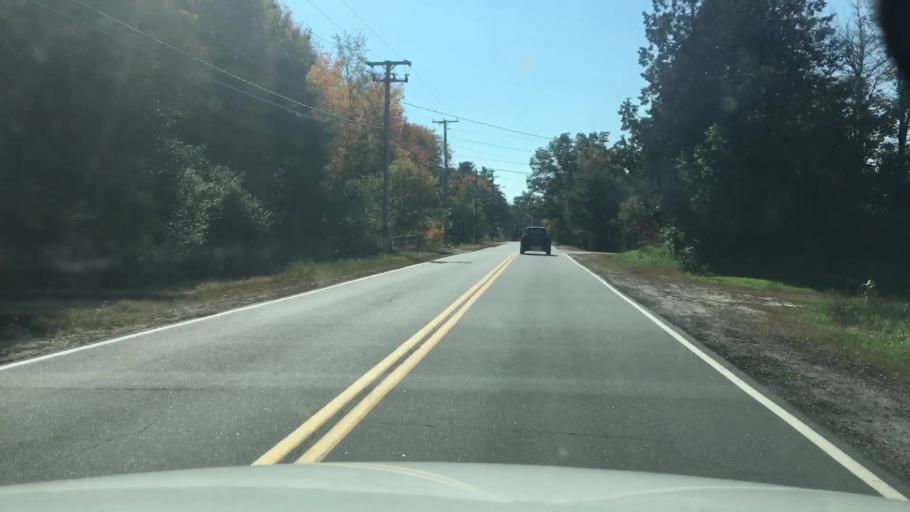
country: US
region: Maine
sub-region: Androscoggin County
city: Lisbon Falls
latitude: 44.0116
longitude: -70.0510
